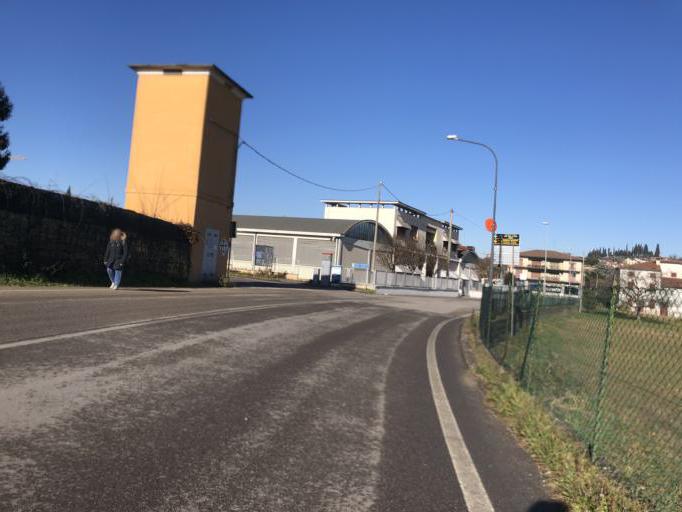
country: IT
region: Veneto
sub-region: Provincia di Verona
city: Sona
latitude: 45.4418
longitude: 10.8214
